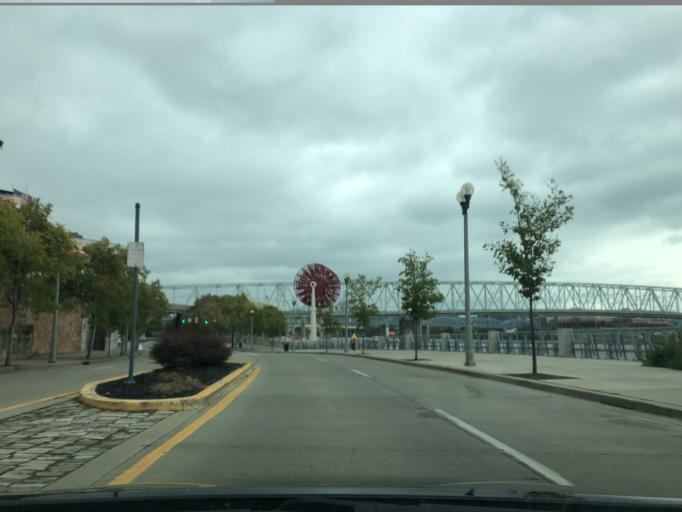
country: US
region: Kentucky
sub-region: Campbell County
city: Newport
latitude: 39.0961
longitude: -84.5067
